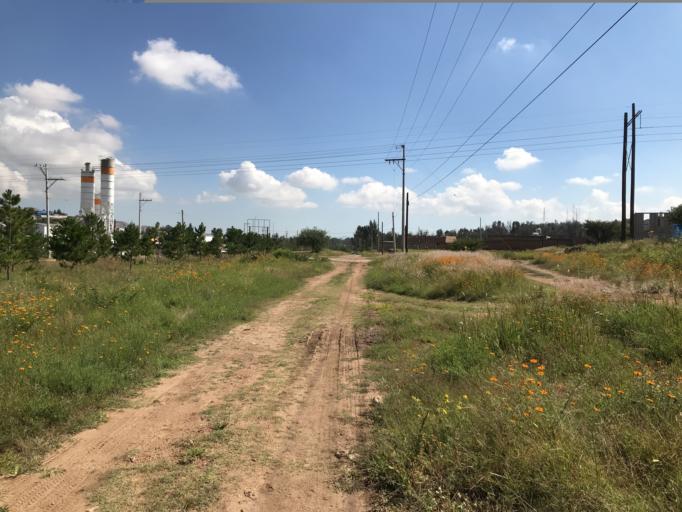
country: MX
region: Durango
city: Victoria de Durango
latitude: 24.0200
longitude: -104.7038
